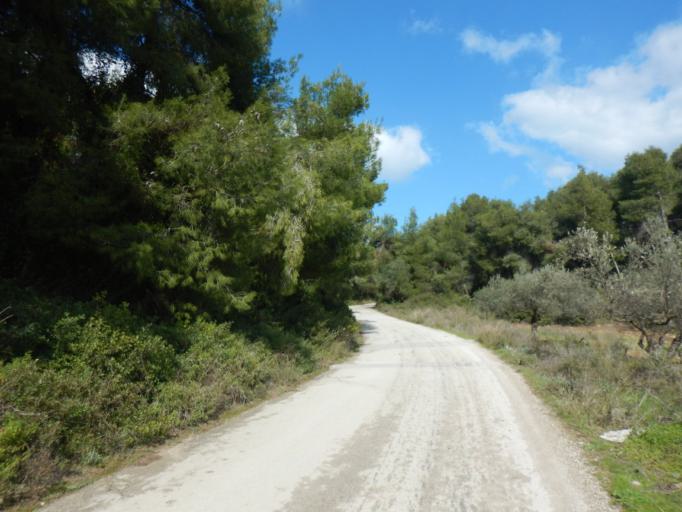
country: GR
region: Attica
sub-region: Nomarchia Anatolikis Attikis
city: Kalamos
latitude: 38.2978
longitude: 23.8478
